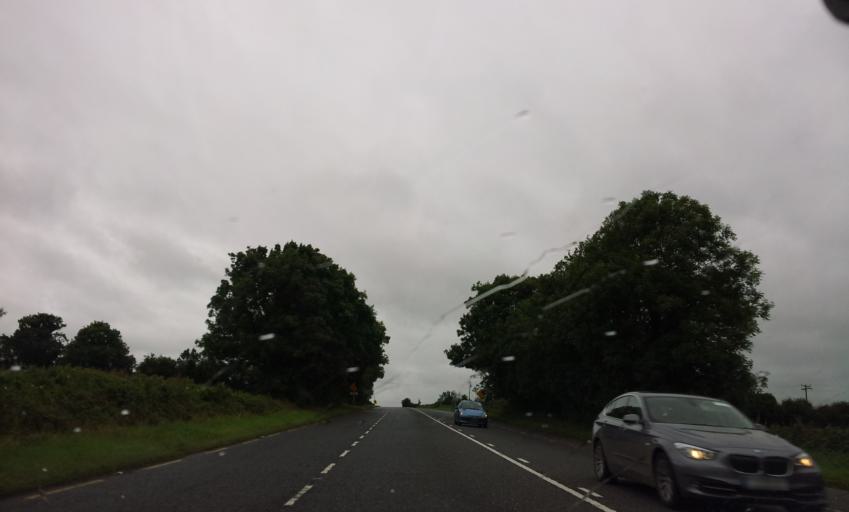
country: IE
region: Munster
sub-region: County Cork
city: Mitchelstown
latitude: 52.2835
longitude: -8.2341
